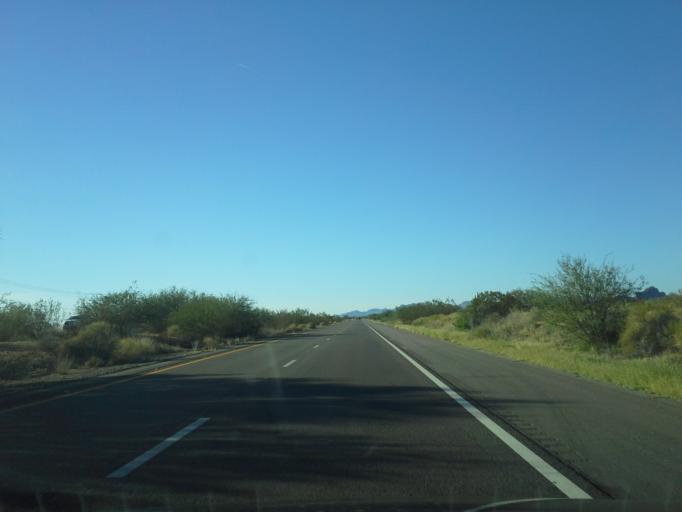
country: US
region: Arizona
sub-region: Pinal County
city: Gold Camp
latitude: 33.3136
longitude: -111.4144
